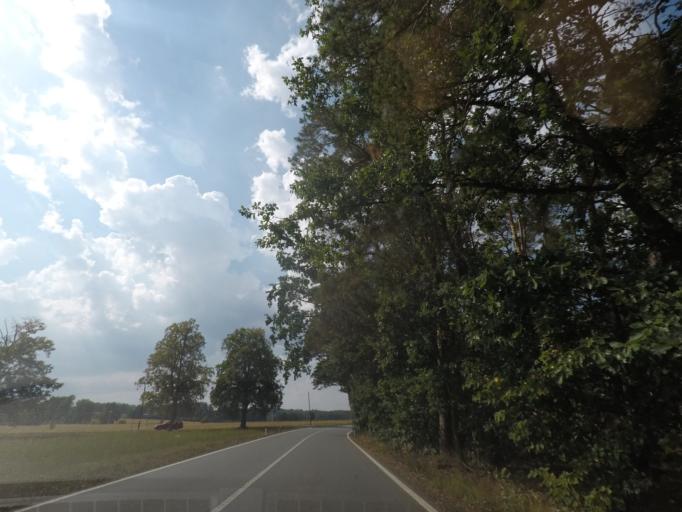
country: CZ
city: Albrechtice nad Orlici
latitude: 50.1326
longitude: 16.0600
